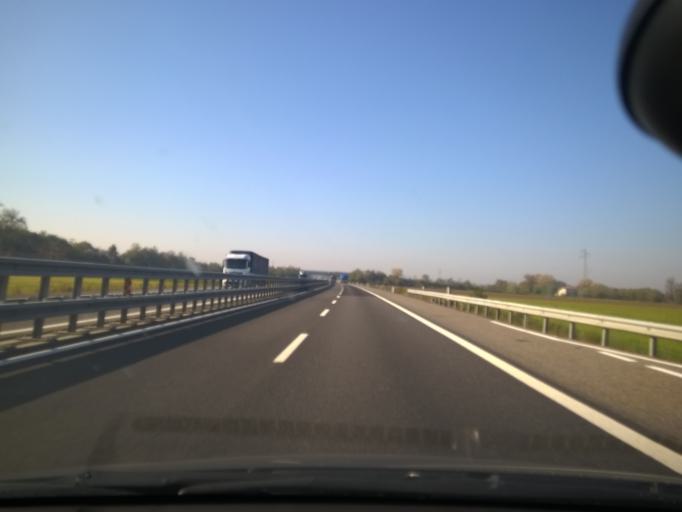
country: IT
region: Emilia-Romagna
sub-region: Provincia di Piacenza
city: Castel San Giovanni
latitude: 45.0789
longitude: 9.4310
